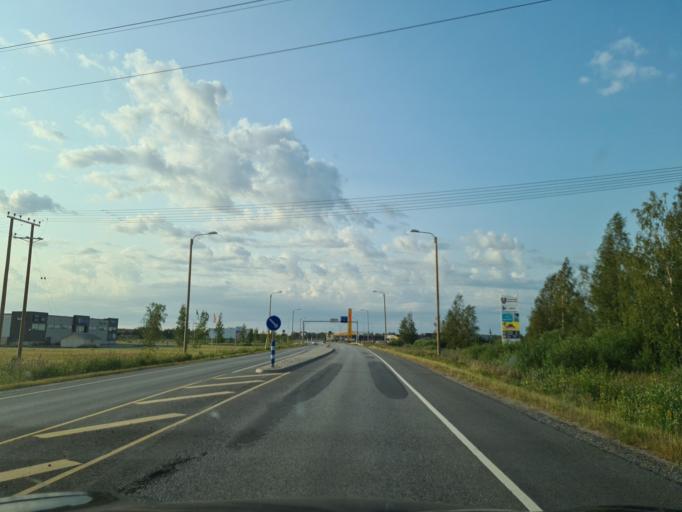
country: FI
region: Southern Ostrobothnia
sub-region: Seinaejoki
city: Kauhava
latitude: 63.0858
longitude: 23.0592
